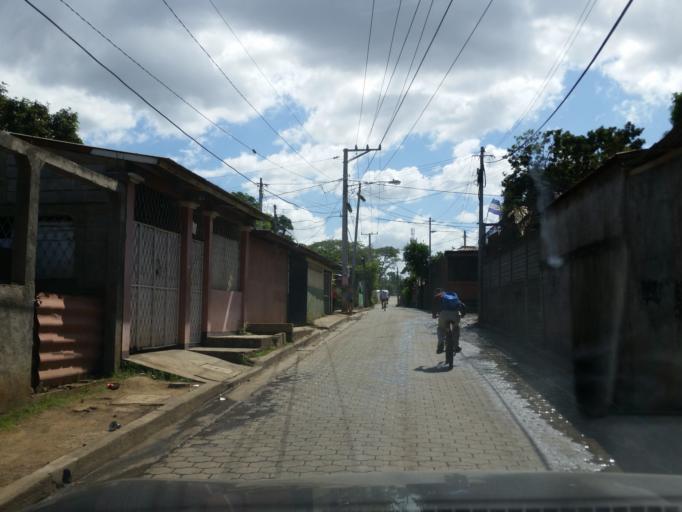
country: NI
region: Managua
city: Managua
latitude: 12.1179
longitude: -86.2243
